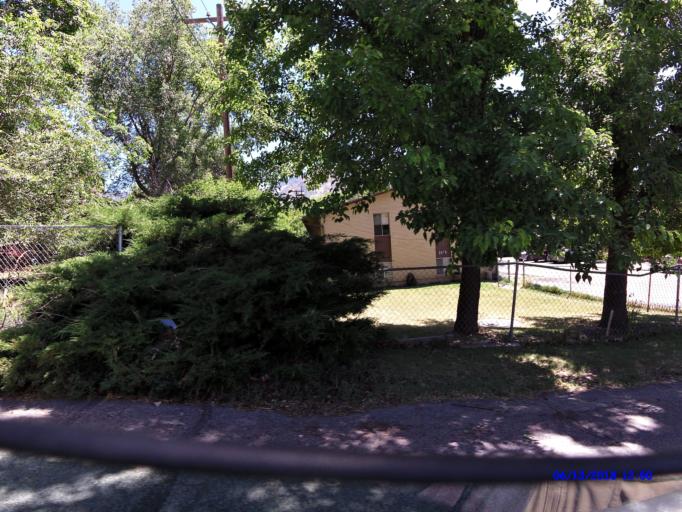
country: US
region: Utah
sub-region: Weber County
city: South Ogden
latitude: 41.2086
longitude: -111.9526
